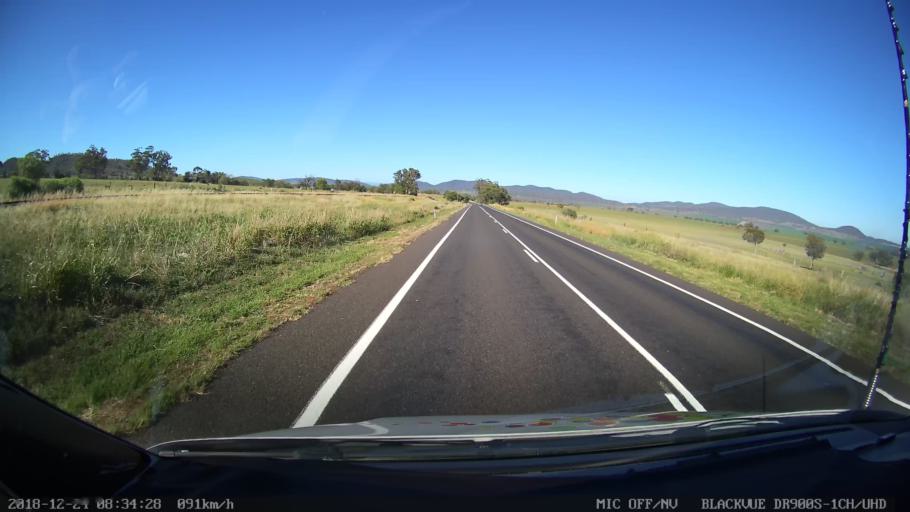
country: AU
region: New South Wales
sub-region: Liverpool Plains
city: Quirindi
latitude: -31.2931
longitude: 150.6705
